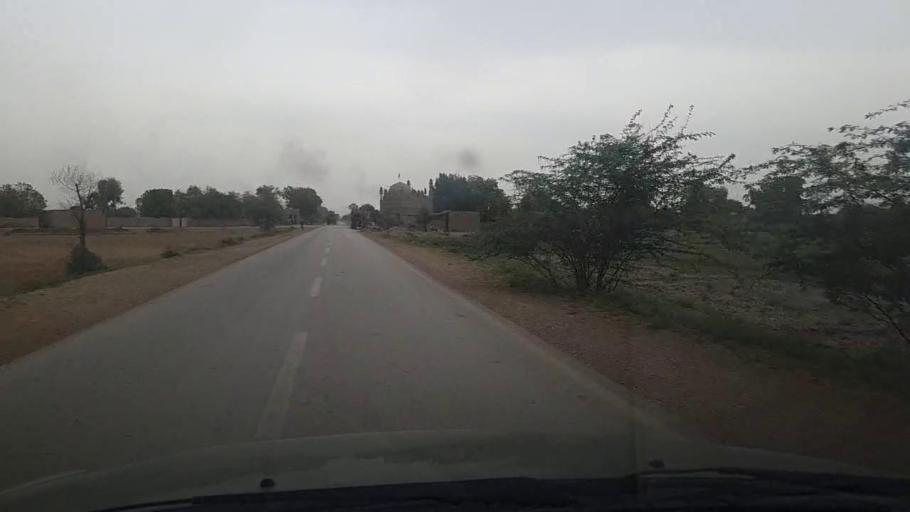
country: PK
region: Sindh
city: Daulatpur
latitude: 26.3356
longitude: 68.1184
